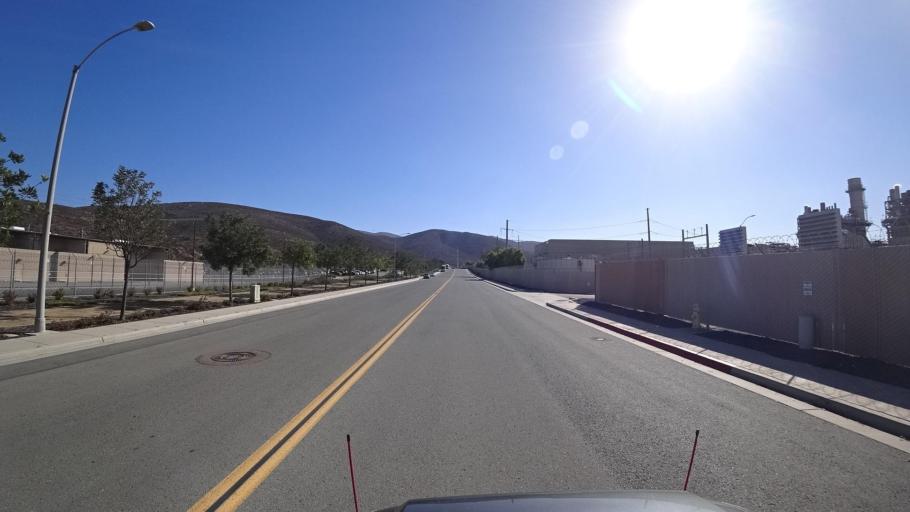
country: MX
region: Baja California
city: Tijuana
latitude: 32.5748
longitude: -116.9151
